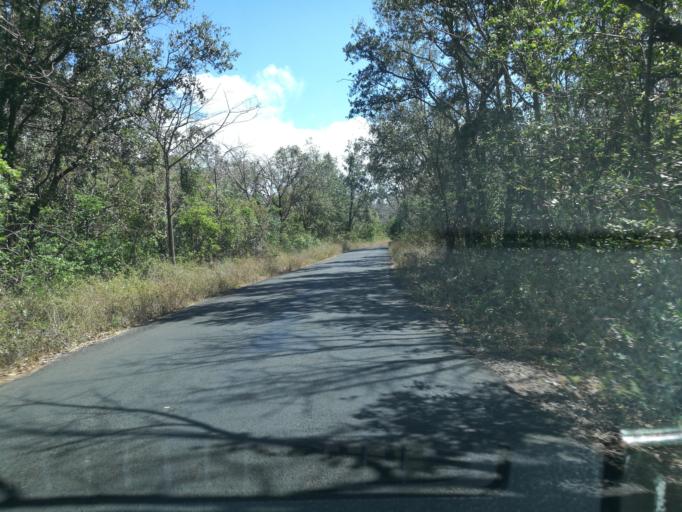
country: CR
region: Guanacaste
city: Liberia
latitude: 10.7494
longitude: -85.3738
